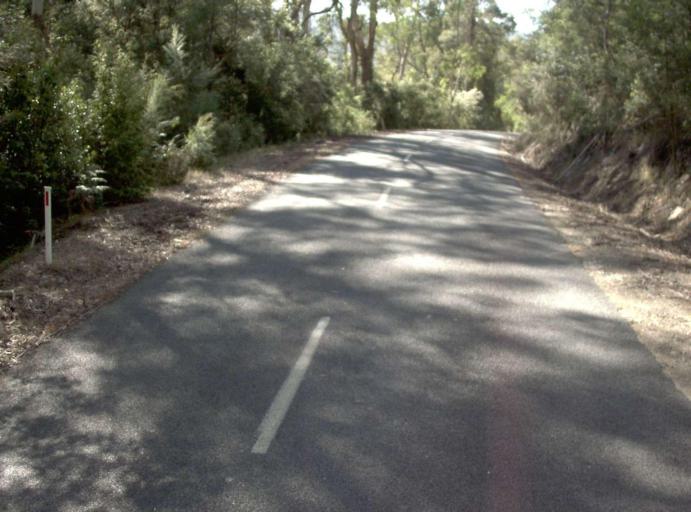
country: AU
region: Victoria
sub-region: East Gippsland
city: Lakes Entrance
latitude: -37.5072
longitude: 148.5370
